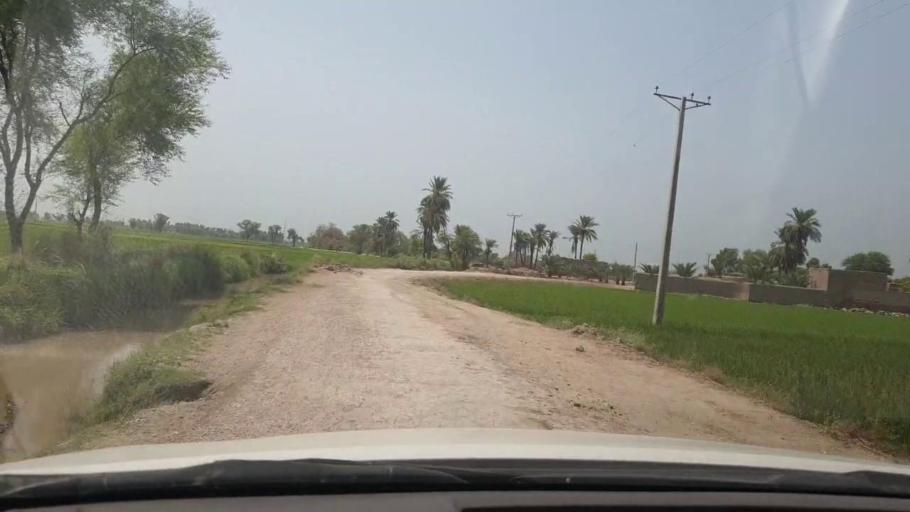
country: PK
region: Sindh
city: Shikarpur
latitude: 28.0088
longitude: 68.6467
